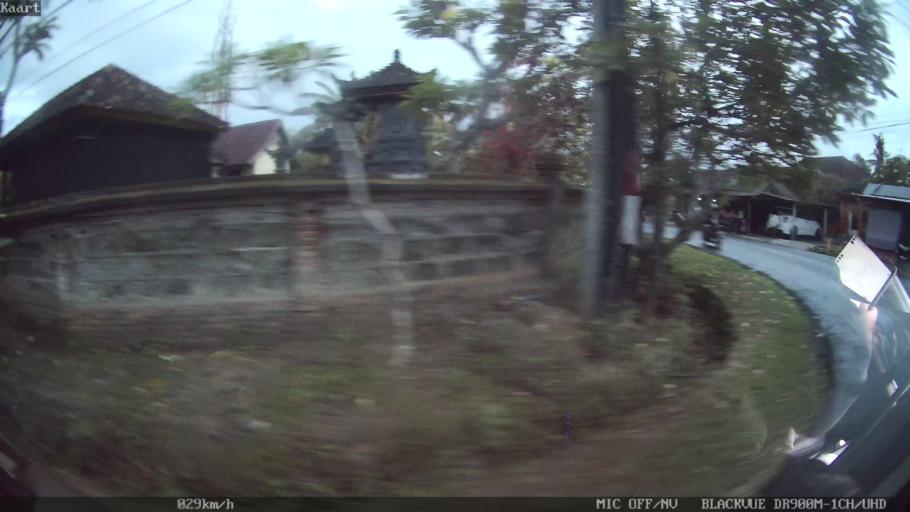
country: ID
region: Bali
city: Banjar Pasekan
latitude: -8.6237
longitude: 115.2760
